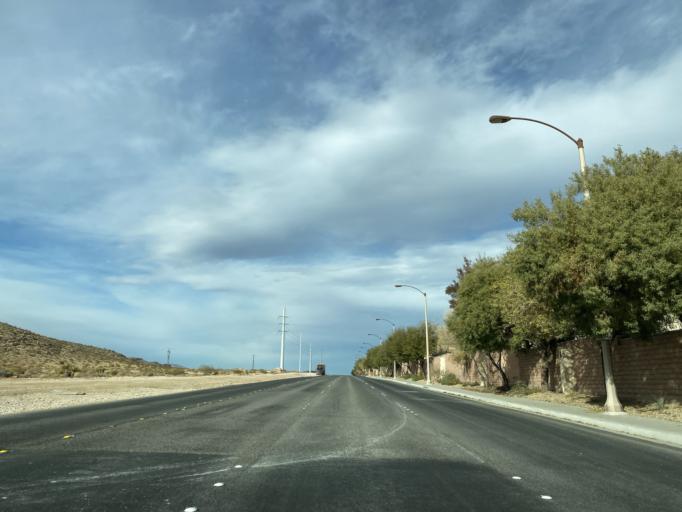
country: US
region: Nevada
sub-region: Clark County
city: Enterprise
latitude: 36.0067
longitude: -115.2981
